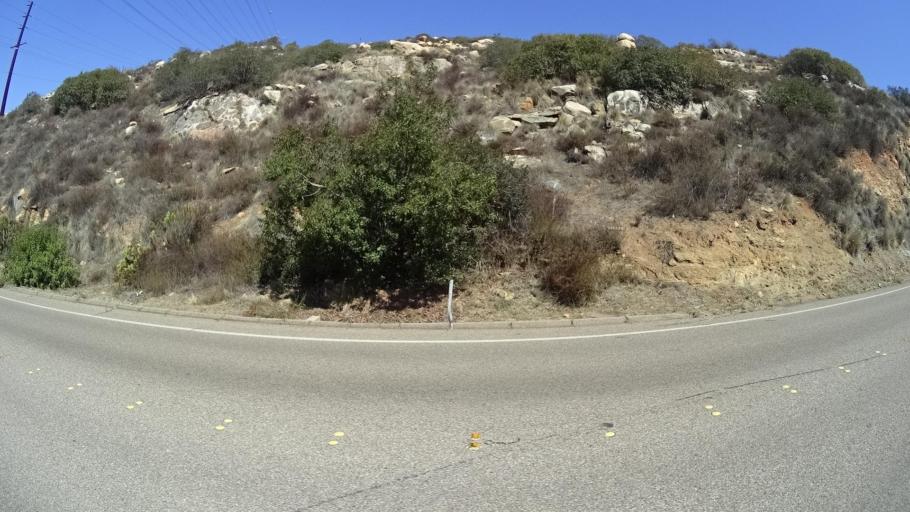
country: US
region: California
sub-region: San Diego County
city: Granite Hills
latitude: 32.8098
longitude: -116.8920
